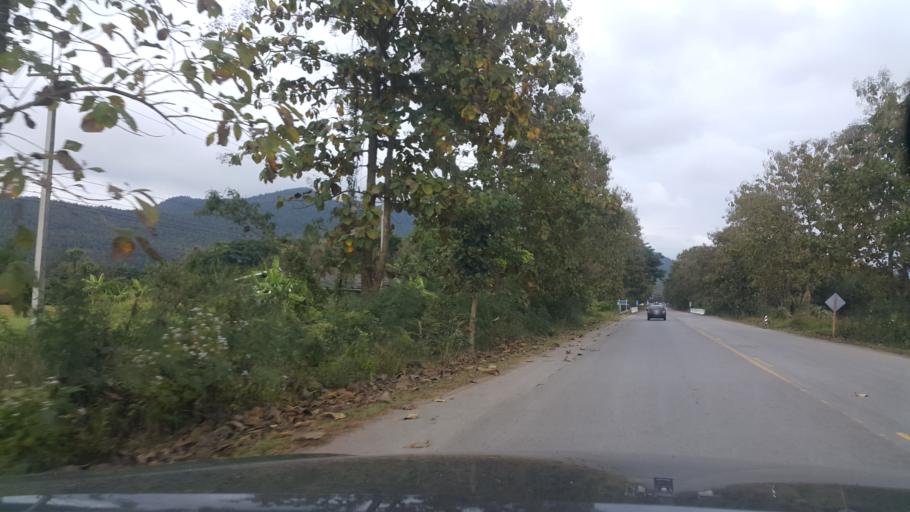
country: TH
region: Chiang Mai
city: Mae On
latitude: 18.7371
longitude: 99.1978
